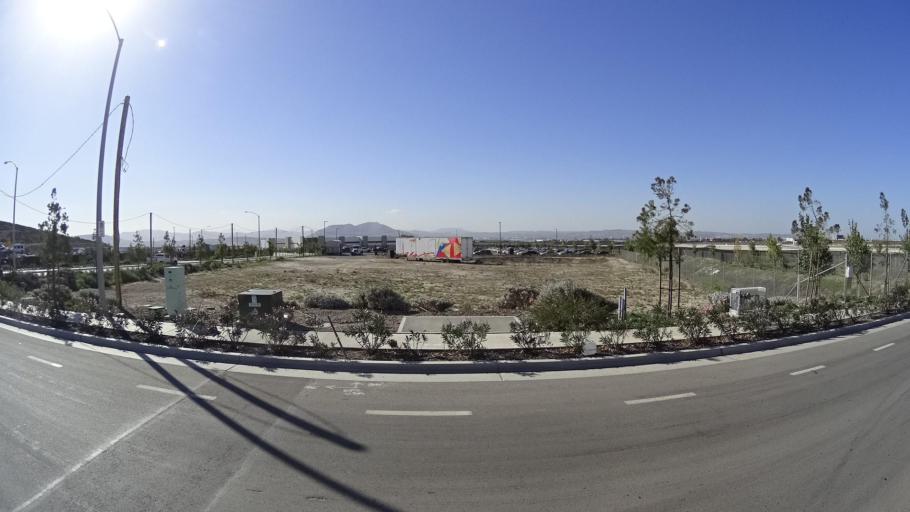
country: MX
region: Baja California
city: Tijuana
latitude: 32.5673
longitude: -116.9133
